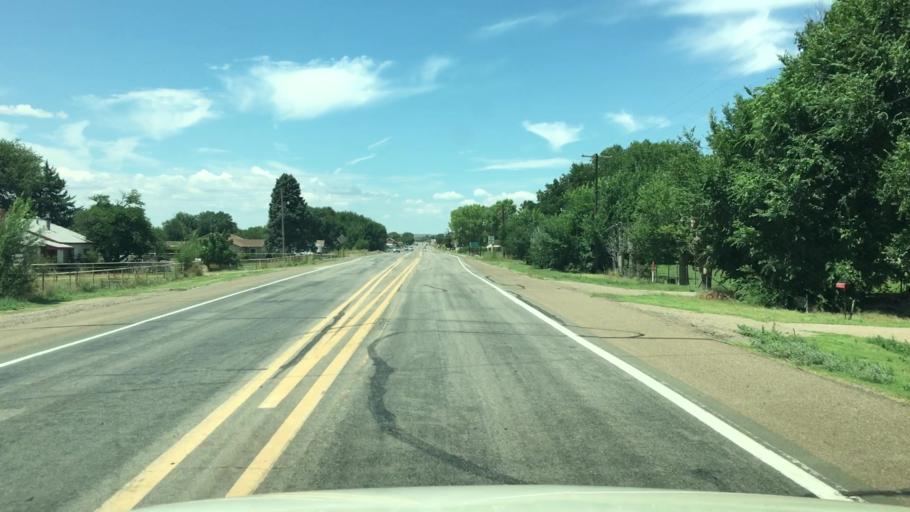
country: US
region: New Mexico
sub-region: De Baca County
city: Fort Sumner
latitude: 34.4644
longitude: -104.2228
